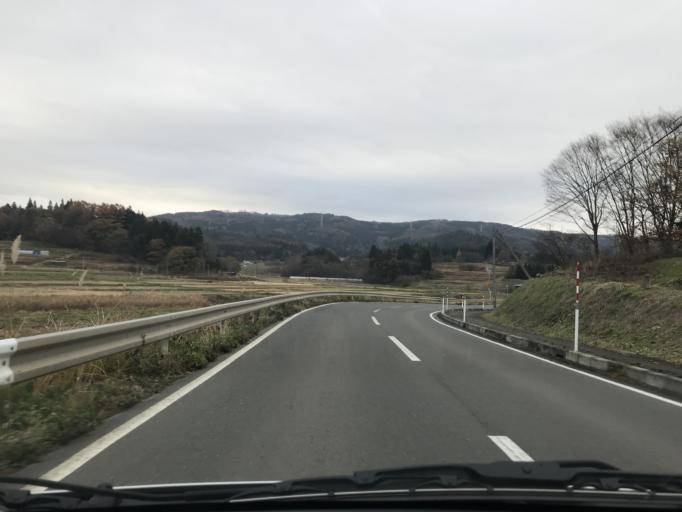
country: JP
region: Iwate
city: Kitakami
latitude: 39.2827
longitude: 141.2649
